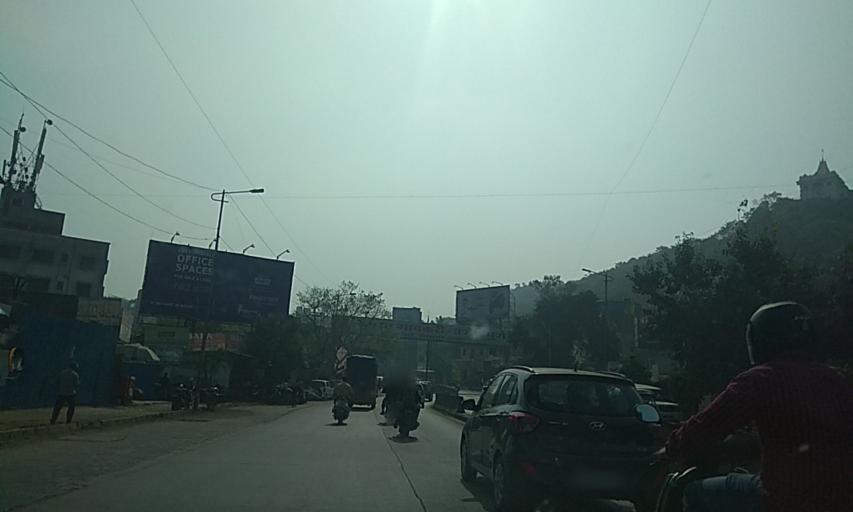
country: IN
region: Maharashtra
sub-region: Pune Division
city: Khadki
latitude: 18.5607
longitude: 73.7882
